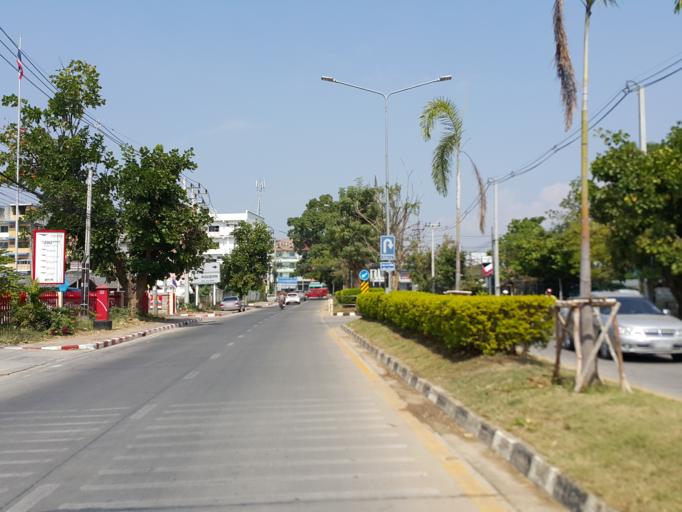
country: TH
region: Chiang Mai
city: Chiang Mai
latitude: 18.8093
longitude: 98.9953
